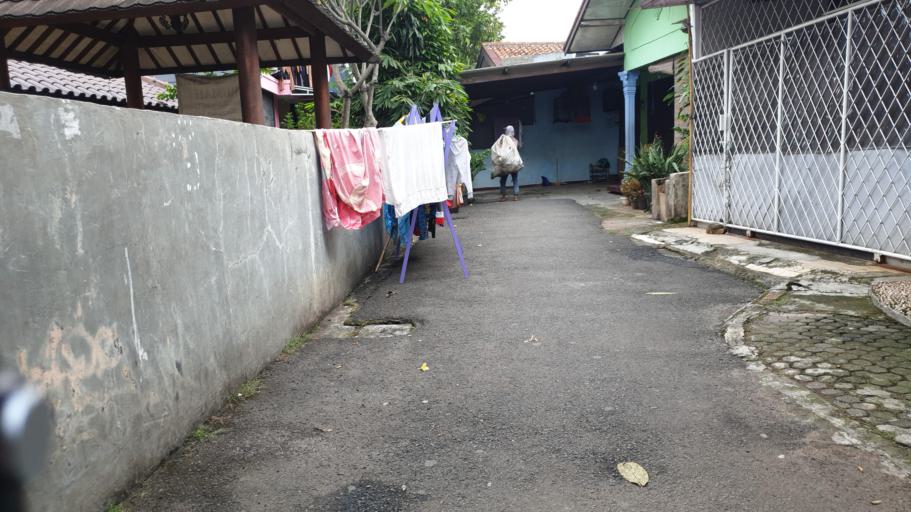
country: ID
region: West Java
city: Pamulang
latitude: -6.3027
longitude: 106.7805
